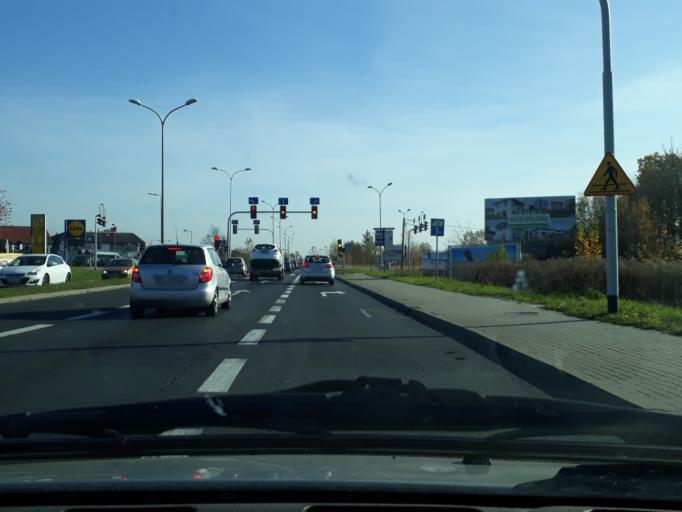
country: PL
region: Silesian Voivodeship
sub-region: Powiat tarnogorski
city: Tarnowskie Gory
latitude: 50.4364
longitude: 18.8449
